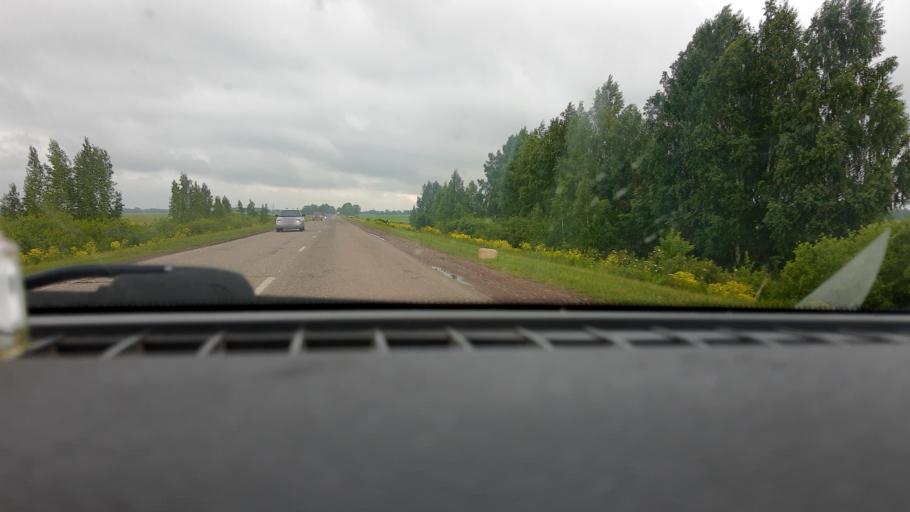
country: RU
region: Bashkortostan
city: Priyutovo
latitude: 53.9253
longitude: 53.9635
